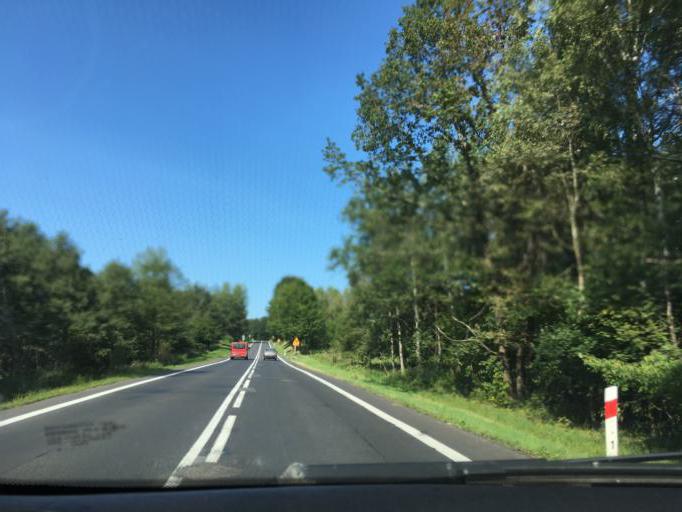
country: PL
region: Subcarpathian Voivodeship
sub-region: Powiat sanocki
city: Zagorz
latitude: 49.5110
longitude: 22.2845
